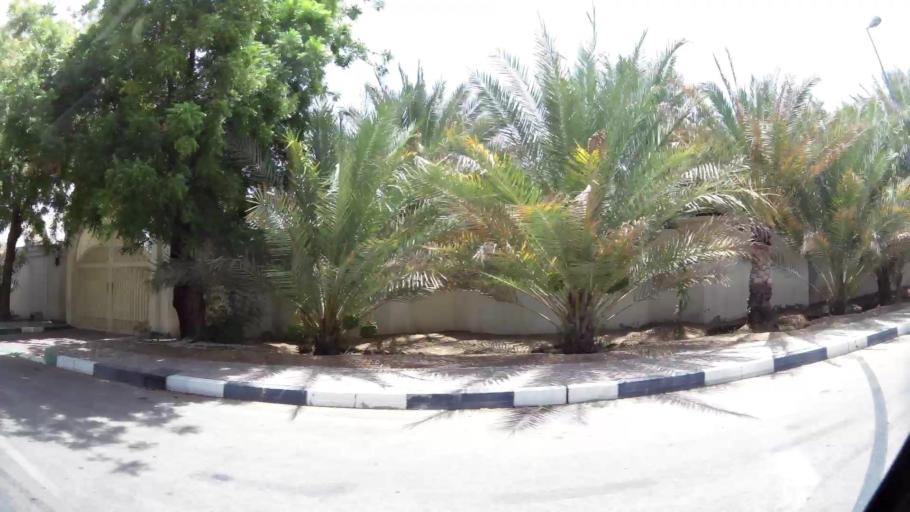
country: AE
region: Abu Dhabi
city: Al Ain
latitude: 24.1940
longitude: 55.7327
